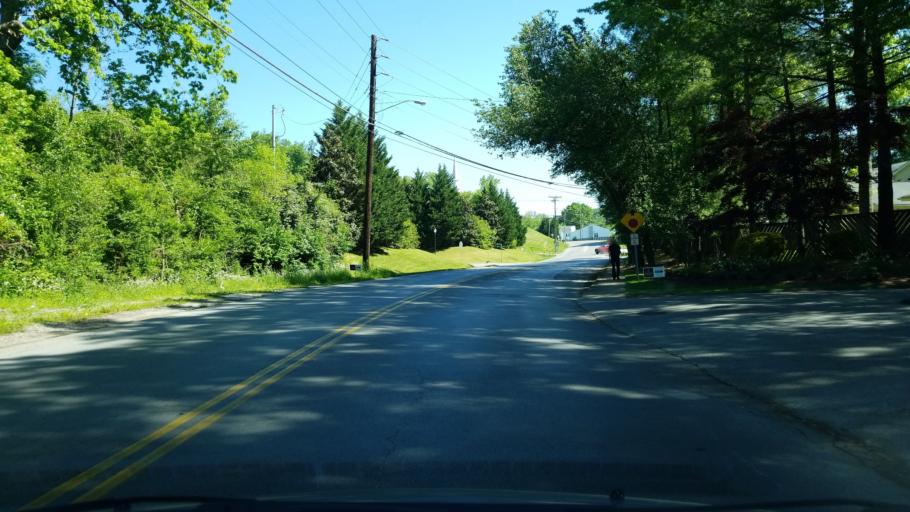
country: US
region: Tennessee
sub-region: Hamilton County
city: Red Bank
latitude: 35.1254
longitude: -85.3110
